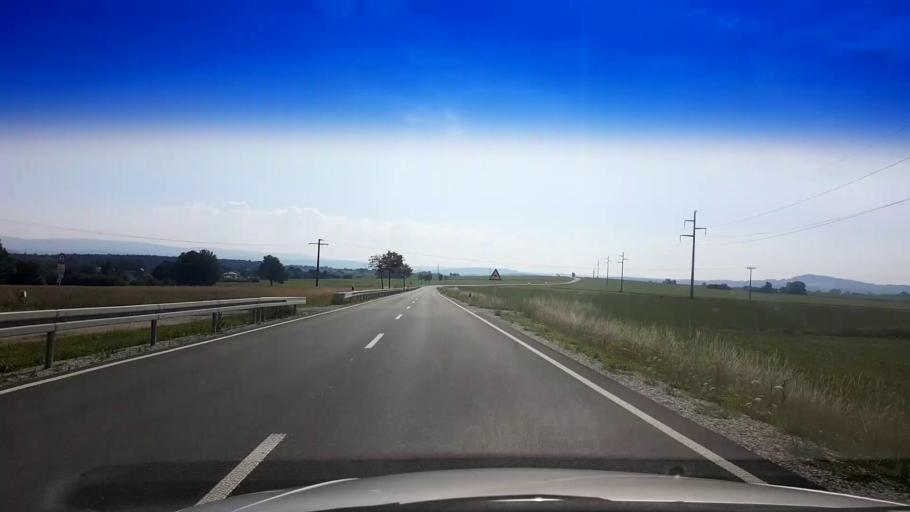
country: DE
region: Bavaria
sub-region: Upper Franconia
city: Mistelgau
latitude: 49.9387
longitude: 11.4572
